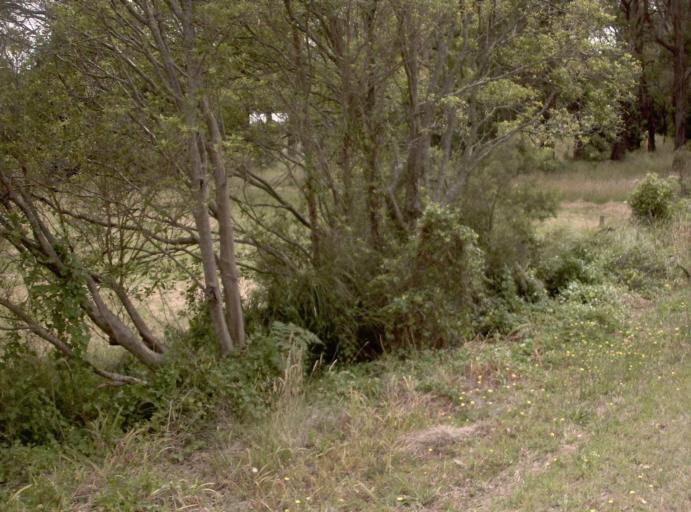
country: AU
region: Victoria
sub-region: Cardinia
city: Koo-Wee-Rup
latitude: -38.3412
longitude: 145.6652
